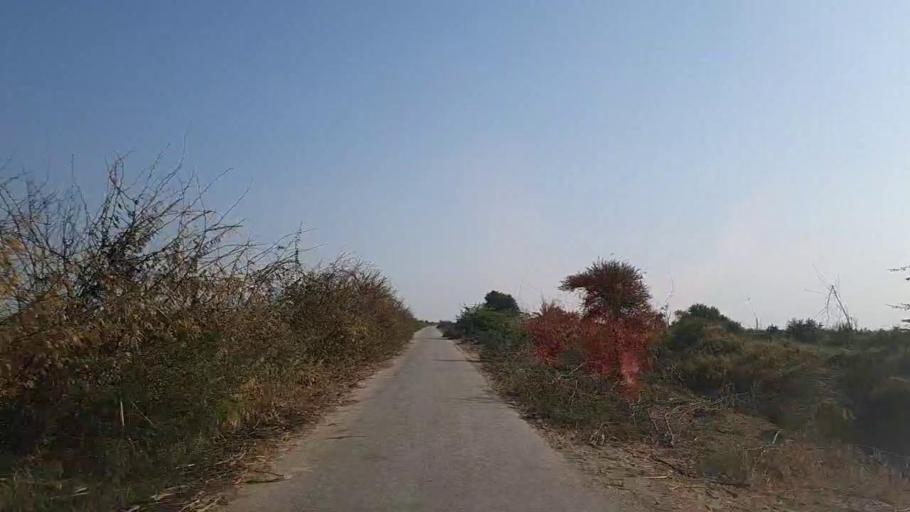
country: PK
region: Sindh
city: Sanghar
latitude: 25.9458
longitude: 69.0508
